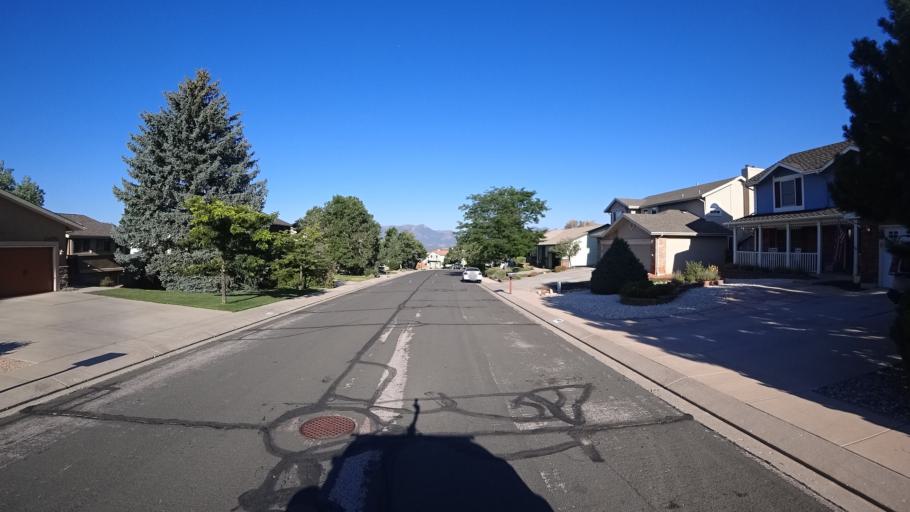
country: US
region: Colorado
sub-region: El Paso County
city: Black Forest
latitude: 38.9561
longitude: -104.7674
